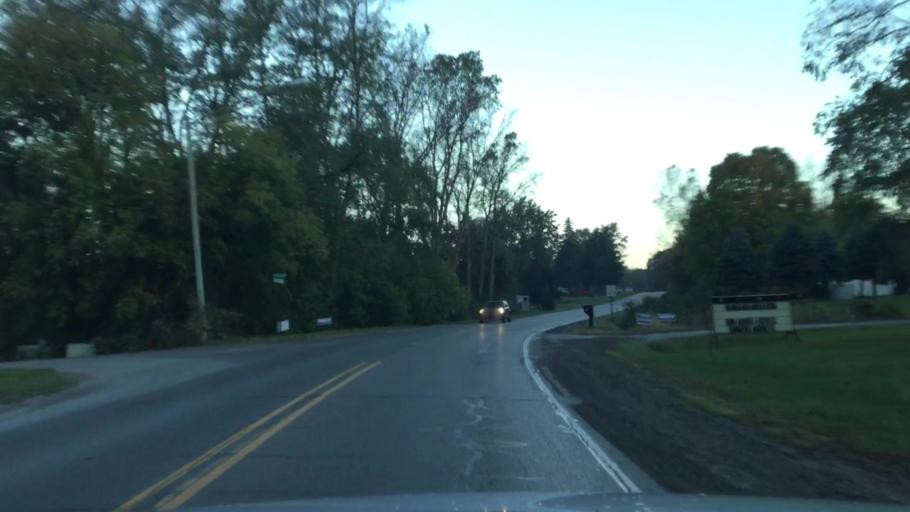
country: US
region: Michigan
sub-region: Livingston County
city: Howell
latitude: 42.6292
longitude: -83.9296
